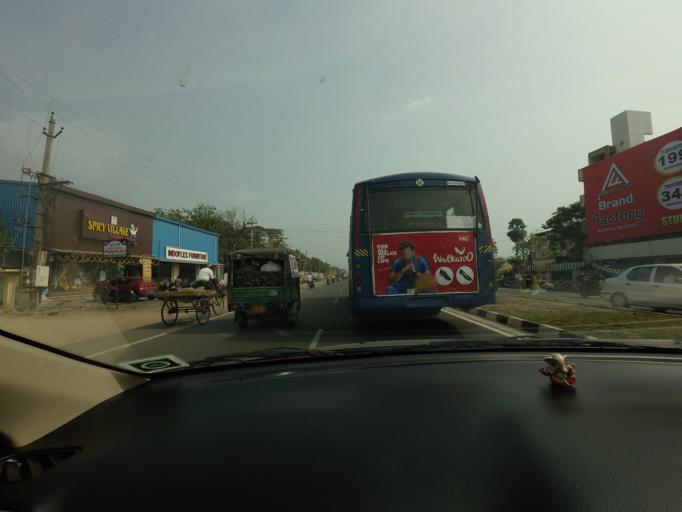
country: IN
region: Andhra Pradesh
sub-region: Krishna
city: Yanamalakuduru
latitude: 16.4826
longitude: 80.6896
